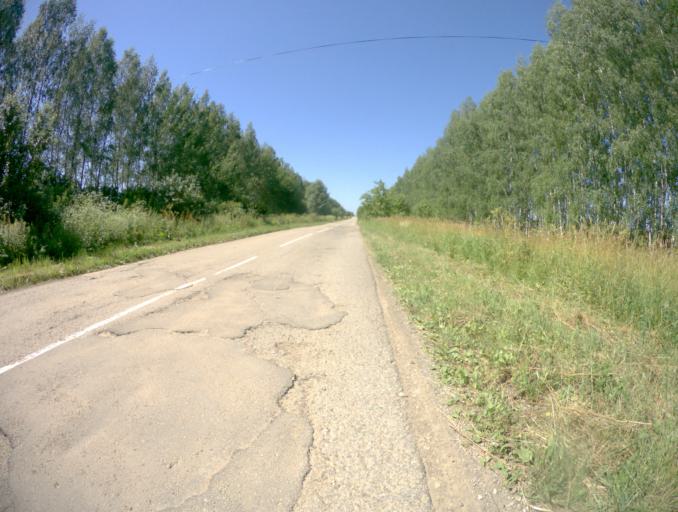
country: RU
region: Nizjnij Novgorod
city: Reshetikha
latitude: 56.1157
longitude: 43.2458
